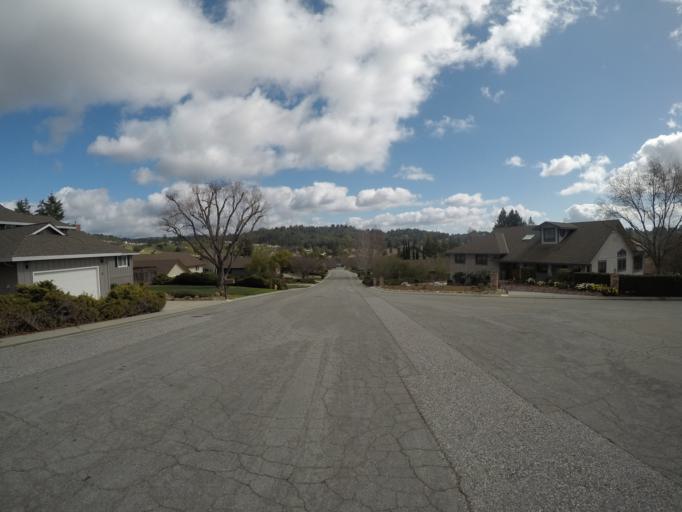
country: US
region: California
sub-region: Santa Cruz County
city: Scotts Valley
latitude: 37.0683
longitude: -122.0096
